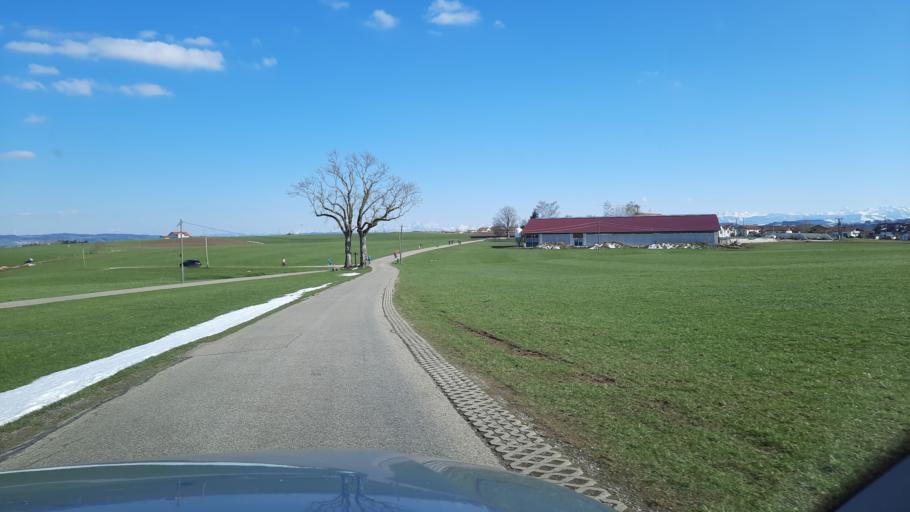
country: DE
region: Bavaria
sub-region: Swabia
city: Altusried
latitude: 47.8147
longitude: 10.2046
